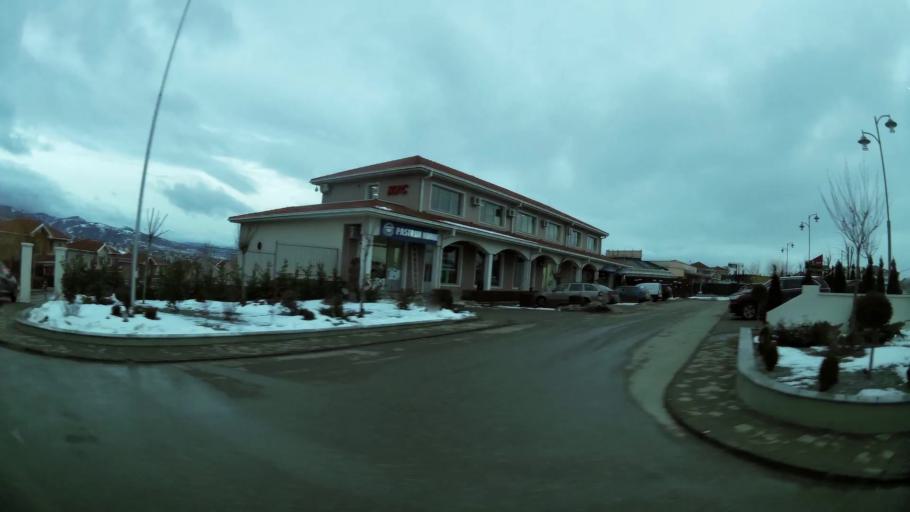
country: XK
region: Pristina
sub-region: Komuna e Prishtines
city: Pristina
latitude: 42.6305
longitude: 21.1675
